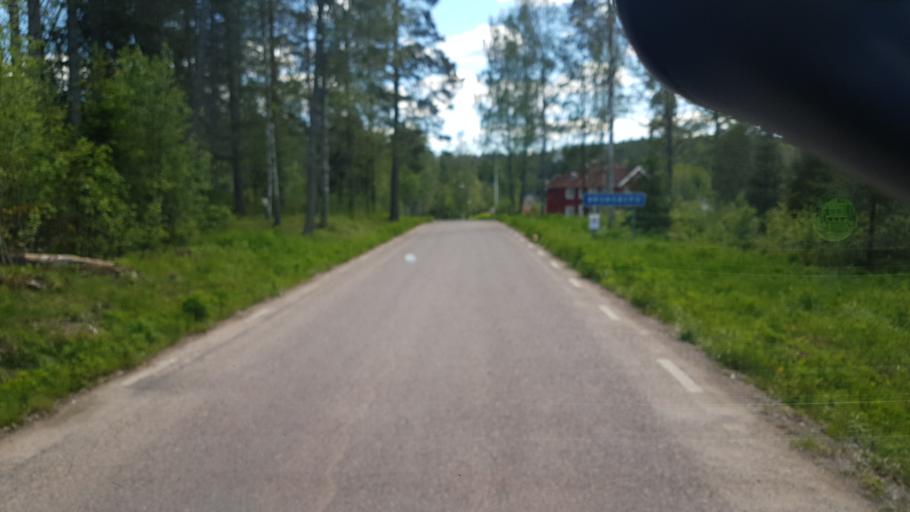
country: SE
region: Vaermland
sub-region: Sunne Kommun
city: Sunne
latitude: 59.6212
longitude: 12.9593
